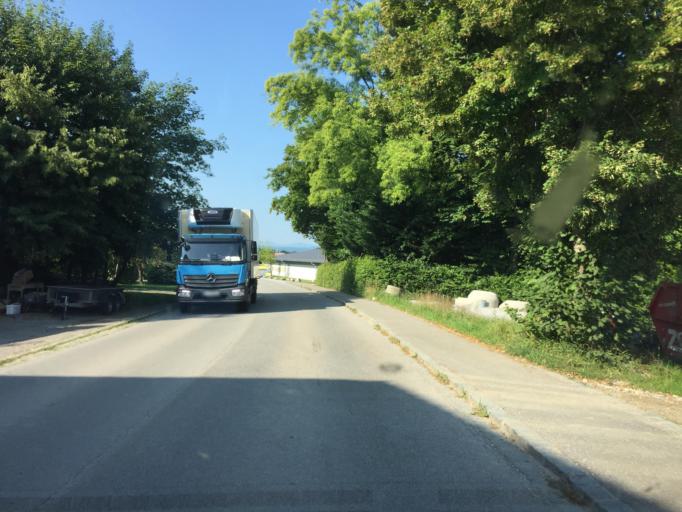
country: DE
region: Bavaria
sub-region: Upper Bavaria
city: Tuntenhausen
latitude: 47.9352
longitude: 12.0133
